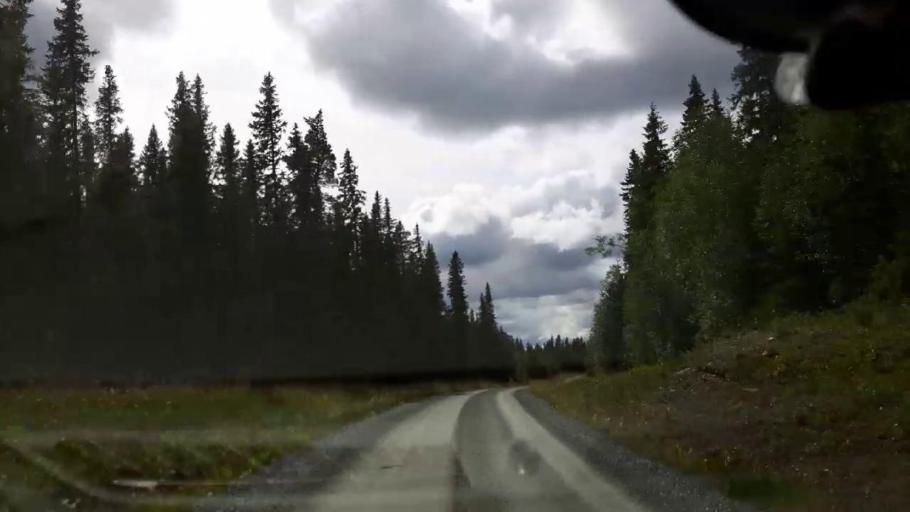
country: SE
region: Jaemtland
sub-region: Krokoms Kommun
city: Valla
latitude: 63.5724
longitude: 13.8797
